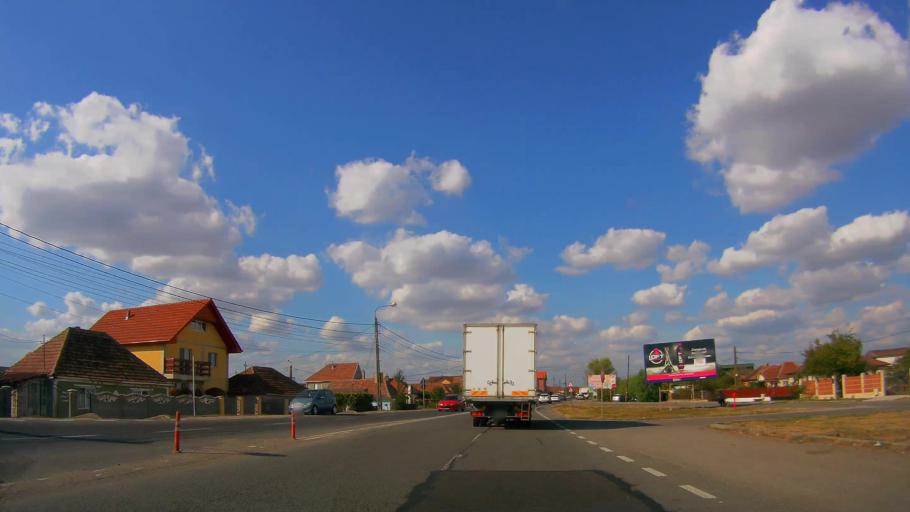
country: RO
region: Satu Mare
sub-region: Oras Ardud
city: Madaras
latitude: 47.7298
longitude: 22.8825
